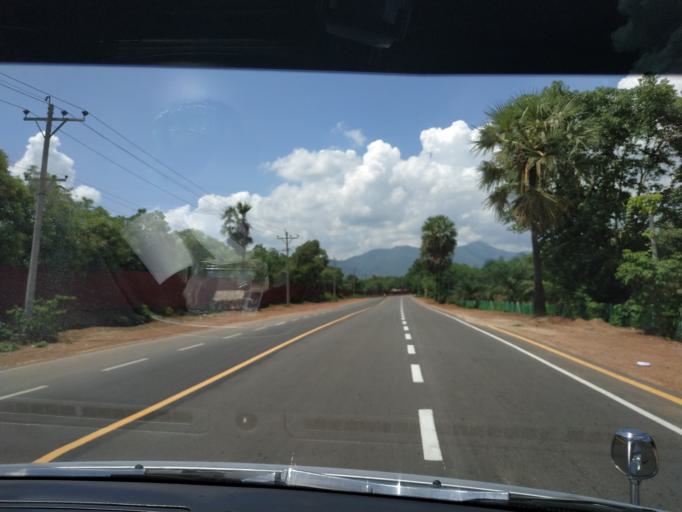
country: MM
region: Mon
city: Kyaikto
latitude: 17.3791
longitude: 97.0534
